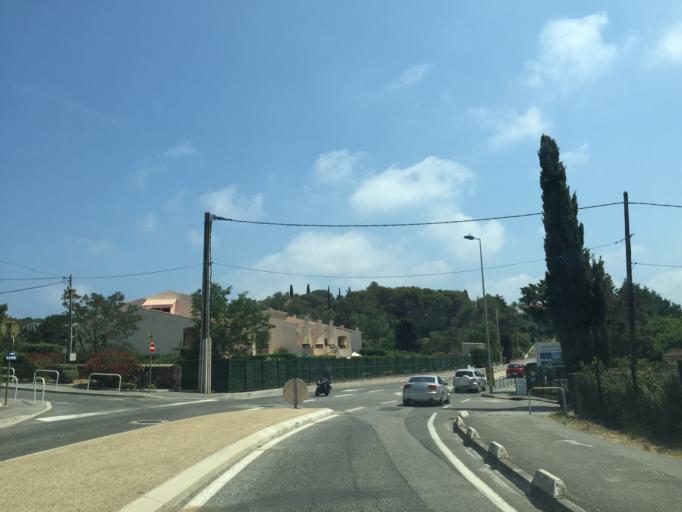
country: FR
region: Provence-Alpes-Cote d'Azur
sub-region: Departement du Var
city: Saint-Raphael
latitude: 43.4305
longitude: 6.8708
